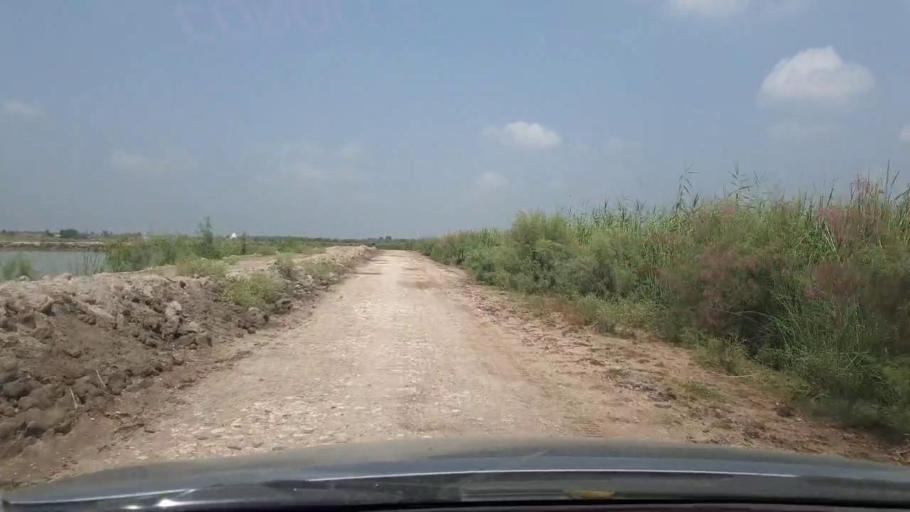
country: PK
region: Sindh
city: Khairpur
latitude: 27.4760
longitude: 68.7008
